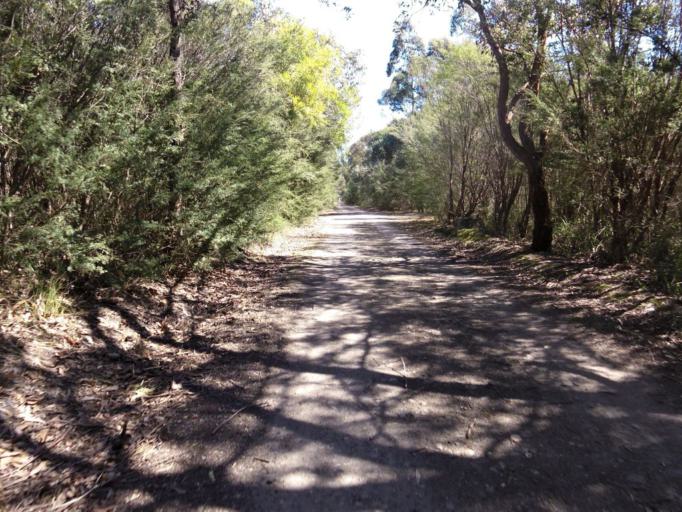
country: AU
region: Victoria
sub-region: Latrobe
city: Moe
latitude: -38.1712
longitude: 146.2989
